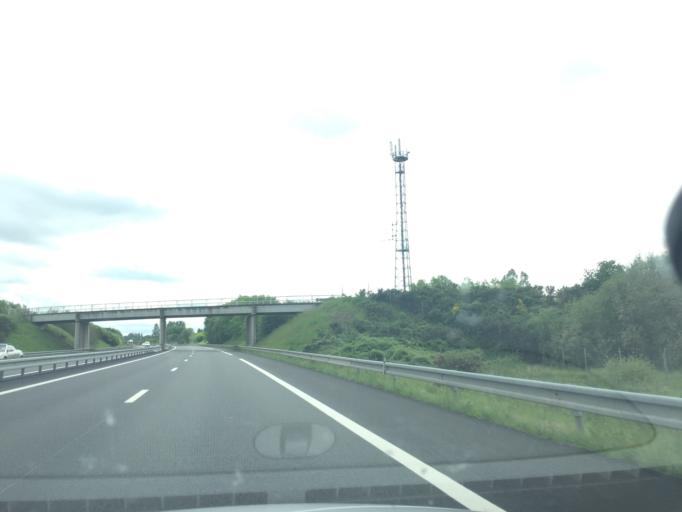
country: FR
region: Pays de la Loire
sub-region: Departement de la Sarthe
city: Brette-les-Pins
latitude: 47.9184
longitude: 0.2999
